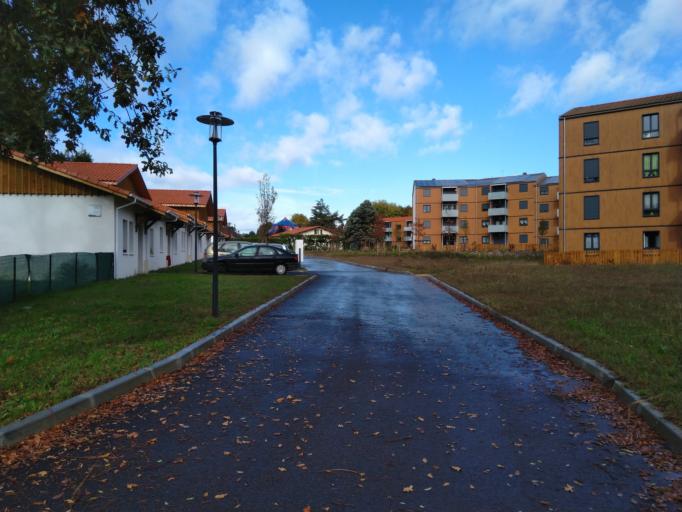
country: FR
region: Aquitaine
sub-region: Departement des Landes
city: Saint-Paul-les-Dax
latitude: 43.7231
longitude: -1.0794
